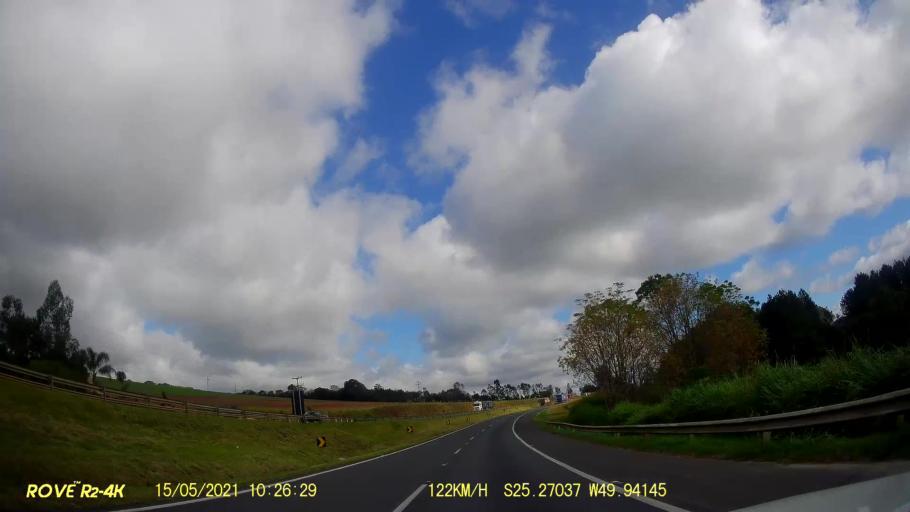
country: BR
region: Parana
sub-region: Palmeira
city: Palmeira
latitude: -25.2702
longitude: -49.9417
